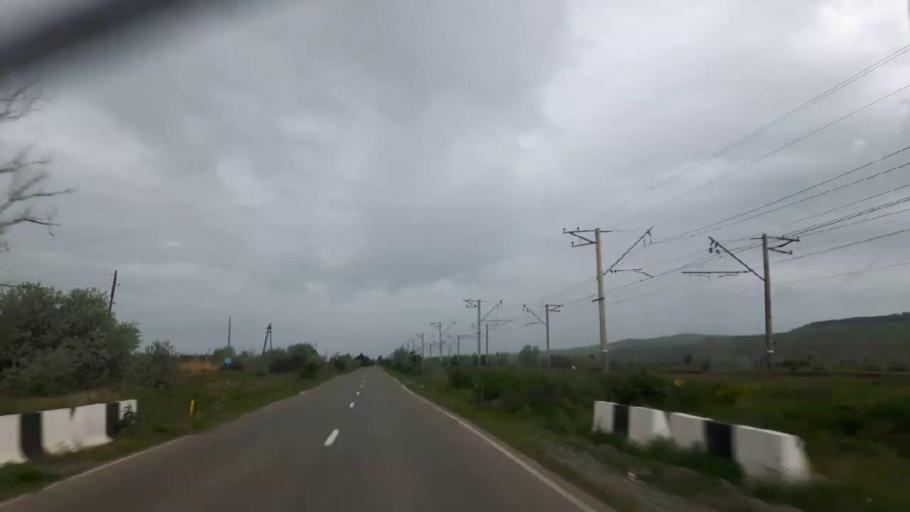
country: GE
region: Shida Kartli
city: Gori
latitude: 41.9961
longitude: 44.0217
